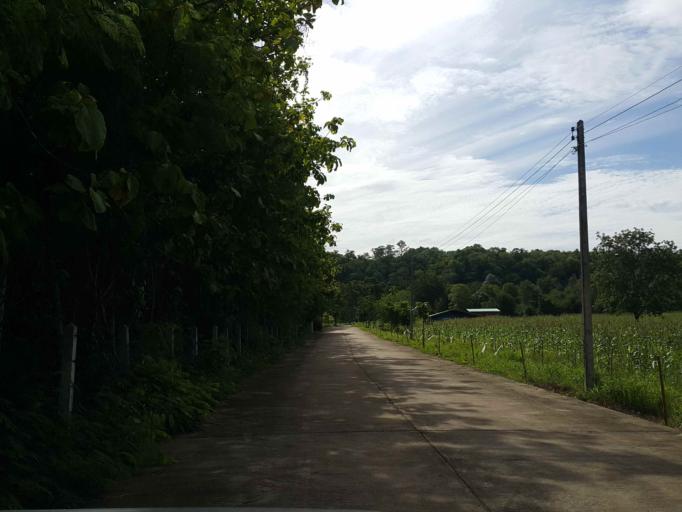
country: TH
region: Sukhothai
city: Thung Saliam
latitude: 17.2278
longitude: 99.5273
